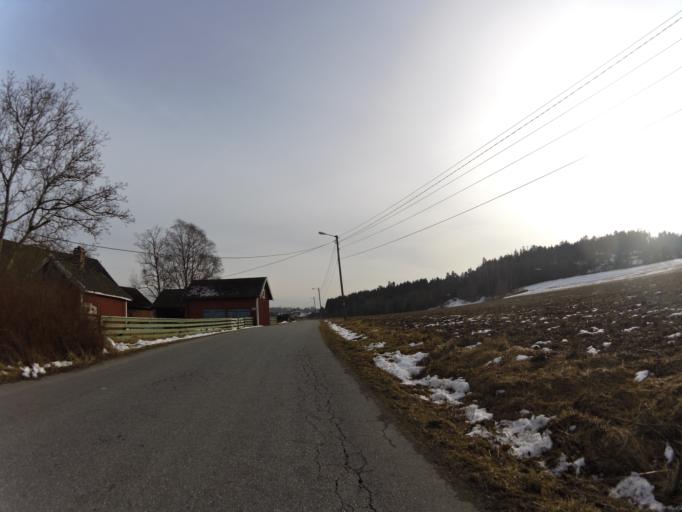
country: NO
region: Ostfold
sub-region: Fredrikstad
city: Fredrikstad
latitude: 59.2778
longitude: 11.0014
